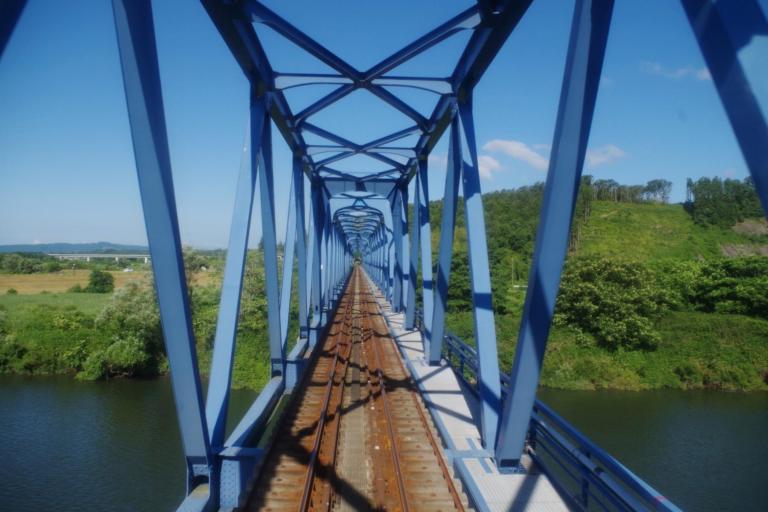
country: JP
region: Miyagi
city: Wakuya
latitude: 38.6088
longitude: 141.2963
